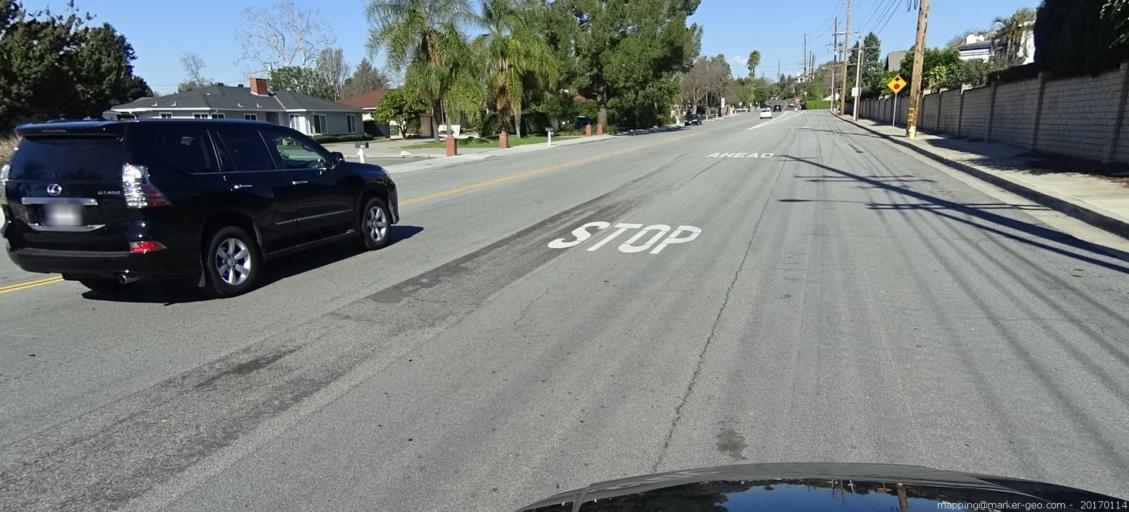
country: US
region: California
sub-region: Orange County
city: North Tustin
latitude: 33.7716
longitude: -117.8054
